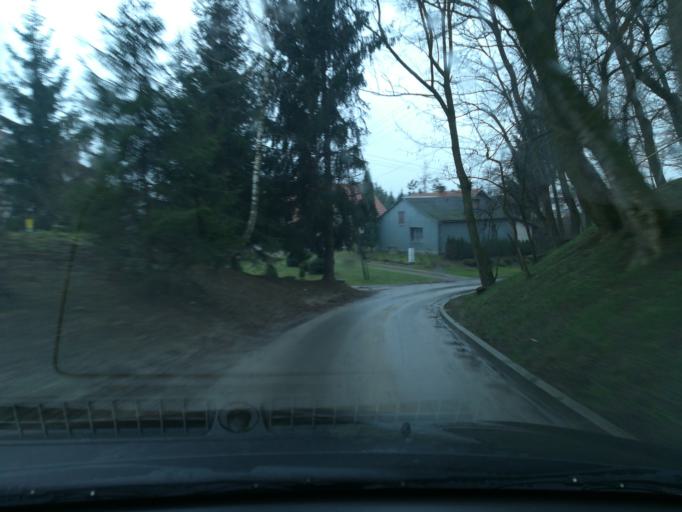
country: PL
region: Subcarpathian Voivodeship
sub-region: Powiat lancucki
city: Kosina
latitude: 50.0694
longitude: 22.3337
